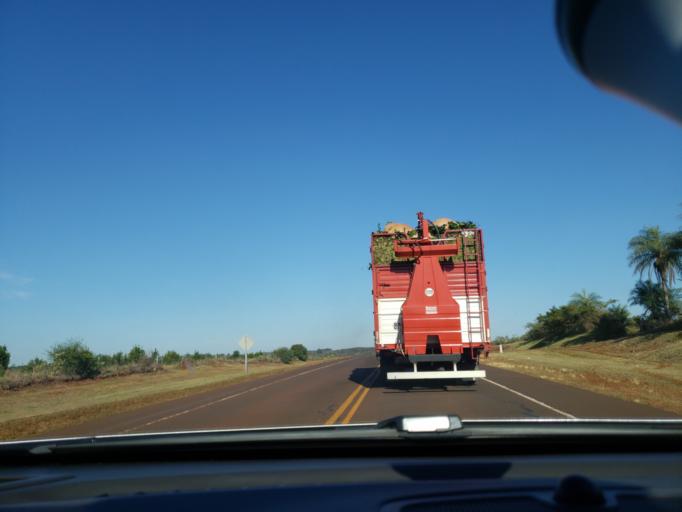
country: AR
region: Misiones
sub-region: Departamento de Apostoles
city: San Jose
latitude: -27.8370
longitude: -55.7686
